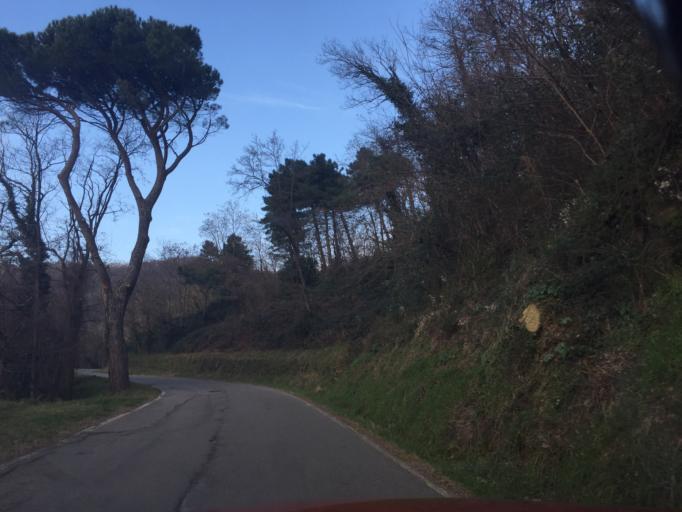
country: IT
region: Tuscany
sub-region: Provincia di Pistoia
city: Larciano
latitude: 43.8305
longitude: 10.9267
